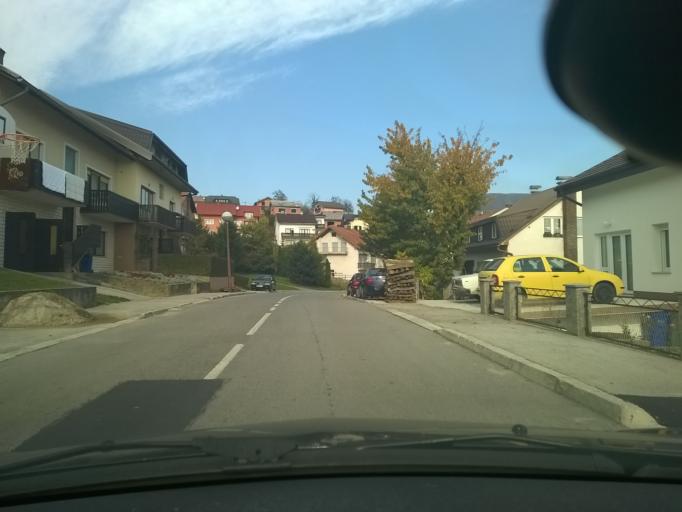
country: HR
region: Krapinsko-Zagorska
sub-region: Grad Krapina
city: Krapina
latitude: 46.1573
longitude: 15.8690
